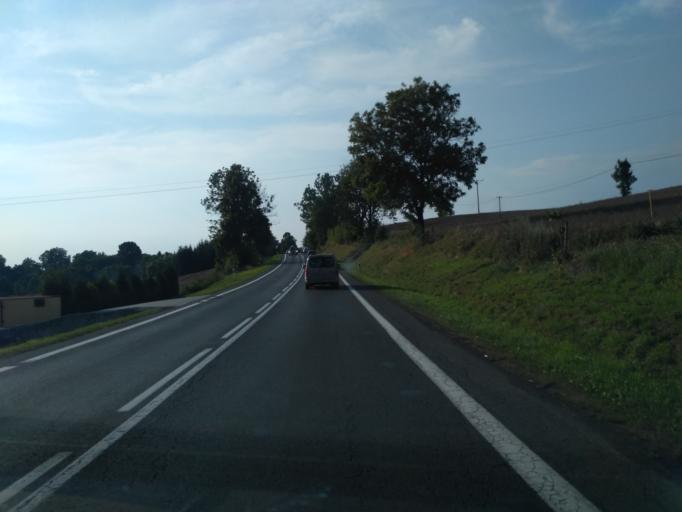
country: PL
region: Subcarpathian Voivodeship
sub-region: Powiat brzozowski
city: Grabownica Starzenska
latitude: 49.6635
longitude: 22.0721
